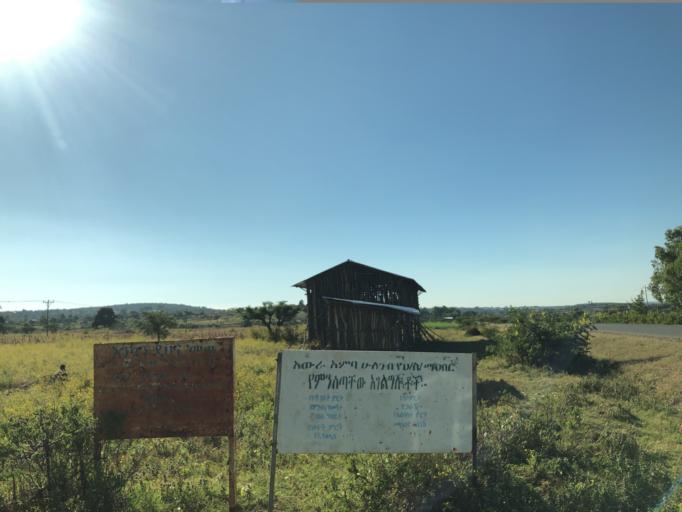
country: ET
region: Amhara
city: Werota
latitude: 11.9366
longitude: 37.7837
